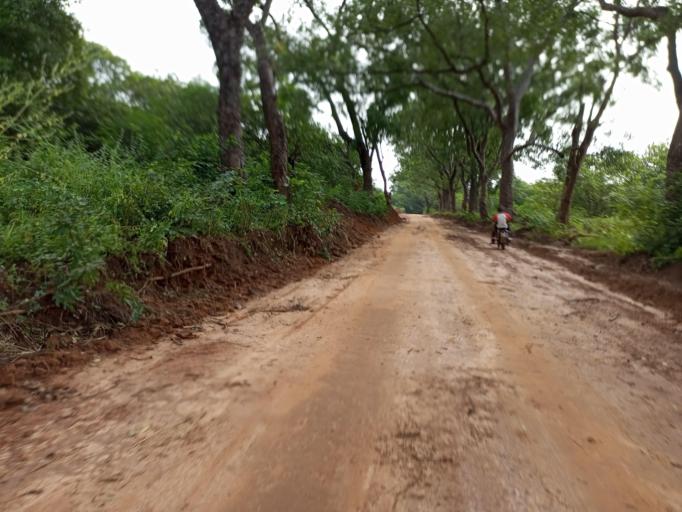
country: GW
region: Oio
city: Bissora
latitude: 12.3921
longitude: -15.6331
